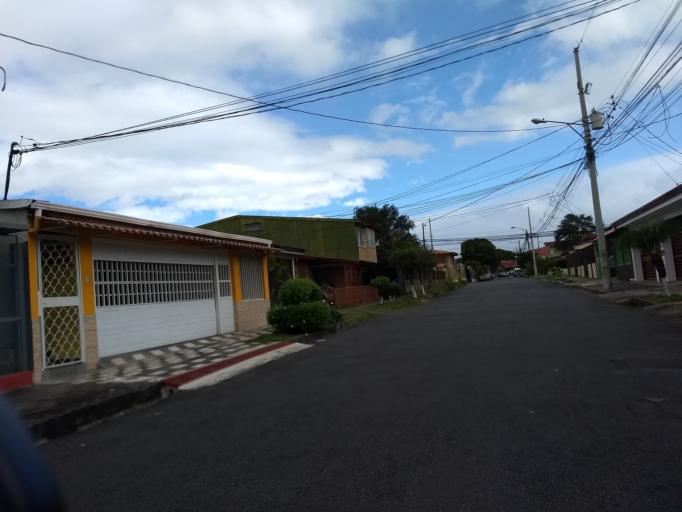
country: CR
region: San Jose
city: San Juan
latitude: 9.9609
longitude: -84.0836
